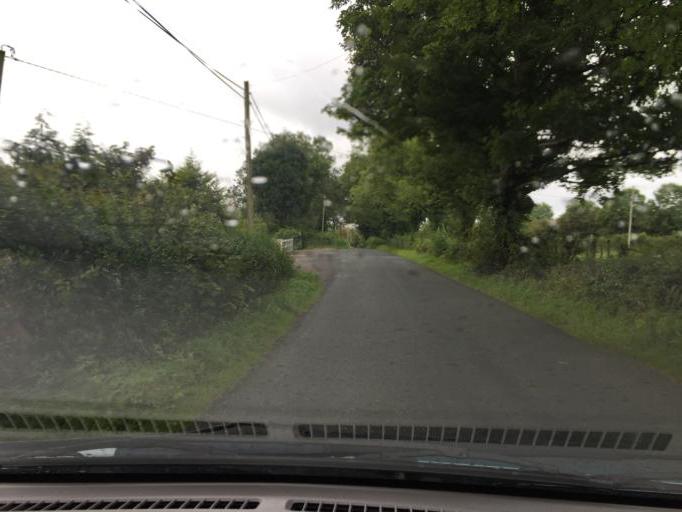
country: IE
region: Connaught
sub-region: Maigh Eo
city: Swinford
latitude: 54.0367
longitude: -8.8746
